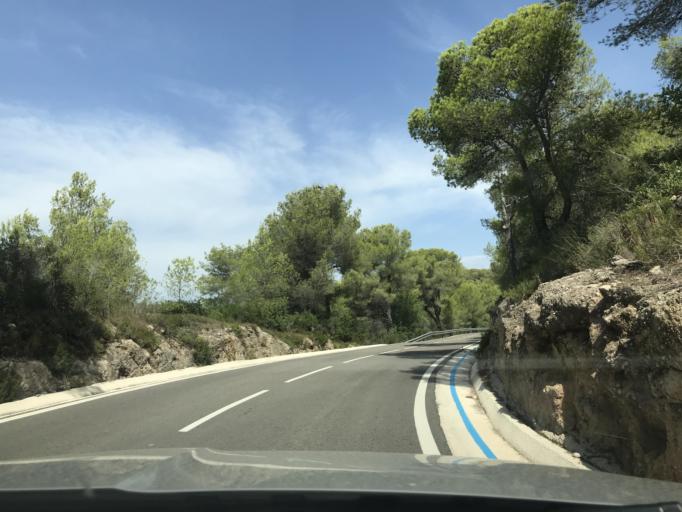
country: ES
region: Catalonia
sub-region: Provincia de Tarragona
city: Salomo
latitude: 41.1934
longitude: 1.3844
